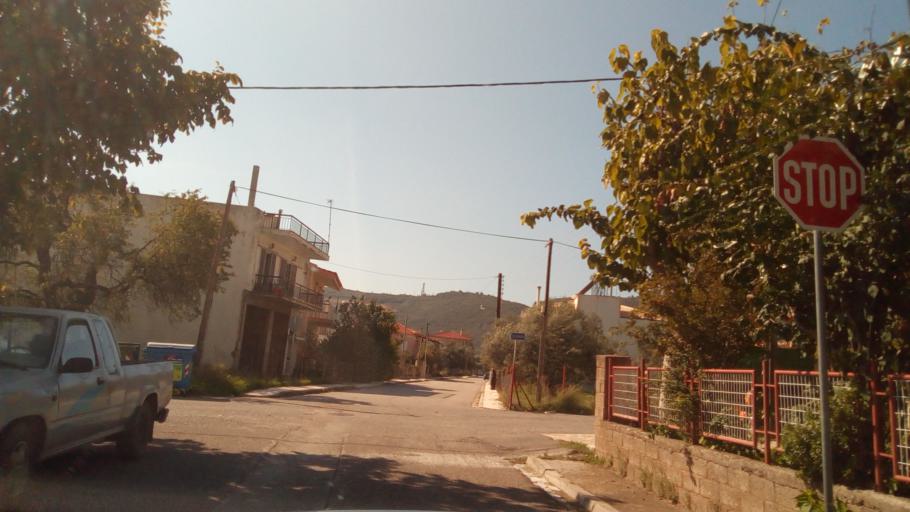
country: GR
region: West Greece
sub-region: Nomos Aitolias kai Akarnanias
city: Nafpaktos
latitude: 38.4077
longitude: 21.8498
